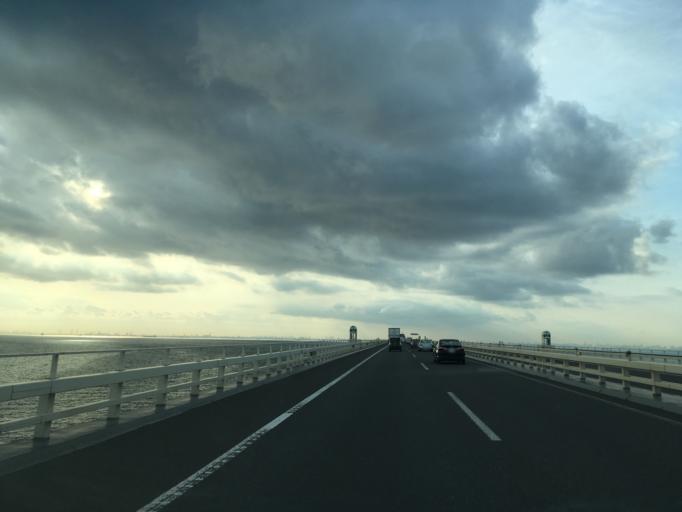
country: JP
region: Chiba
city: Kisarazu
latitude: 35.4438
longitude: 139.9045
